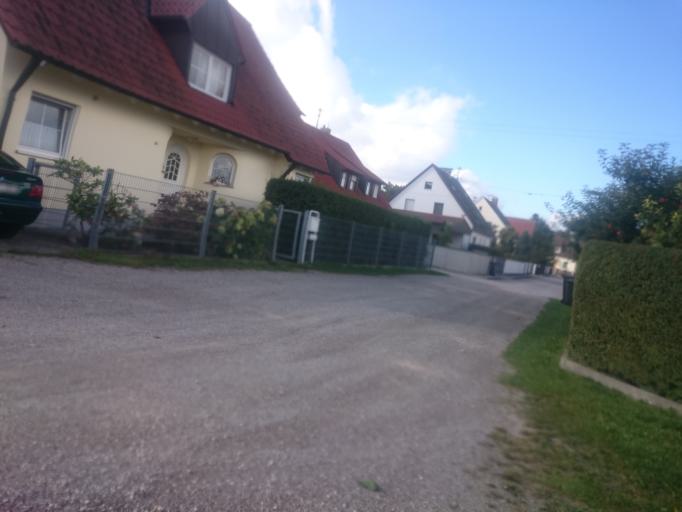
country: DE
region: Bavaria
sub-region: Swabia
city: Friedberg
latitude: 48.3774
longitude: 10.9475
